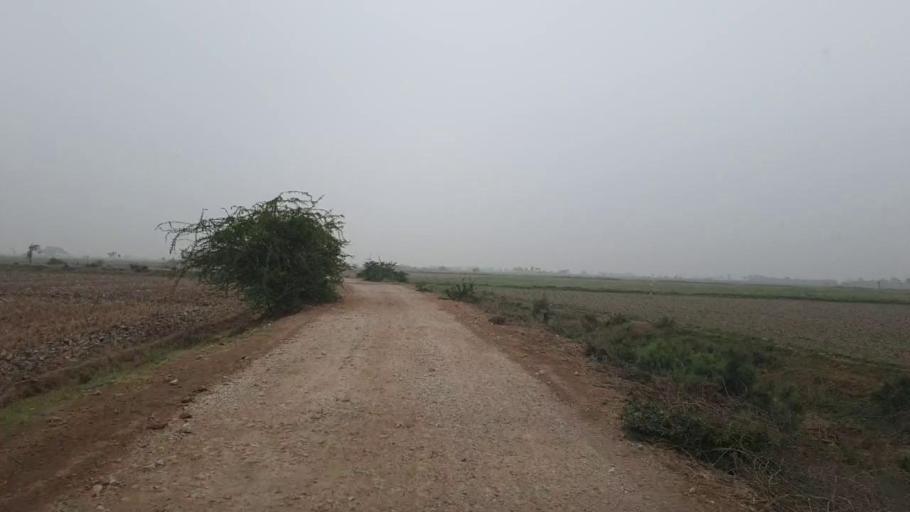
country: PK
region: Sindh
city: Badin
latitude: 24.6281
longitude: 68.6968
